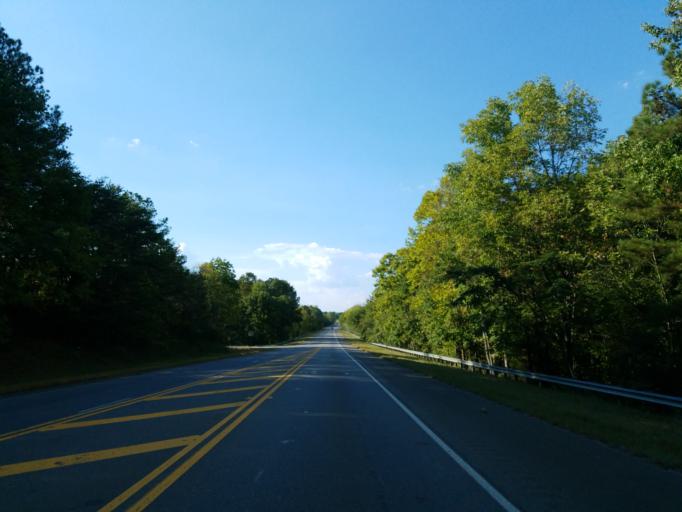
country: US
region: Georgia
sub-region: Murray County
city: Chatsworth
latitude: 34.6888
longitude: -84.7324
